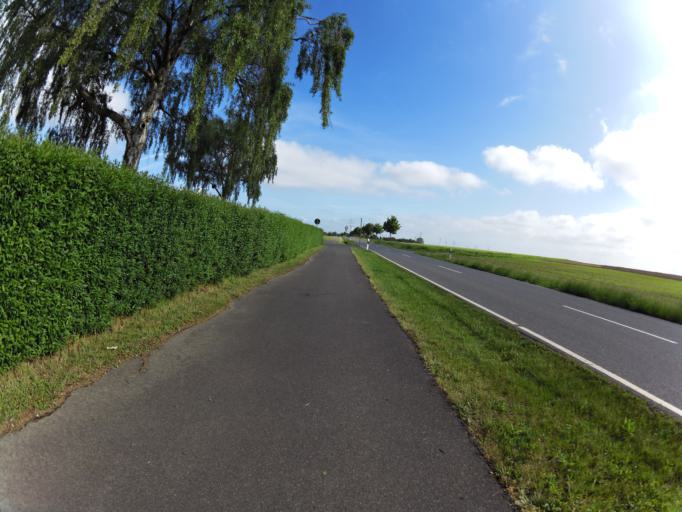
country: DE
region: North Rhine-Westphalia
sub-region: Regierungsbezirk Koln
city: Linnich
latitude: 50.9662
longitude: 6.2186
